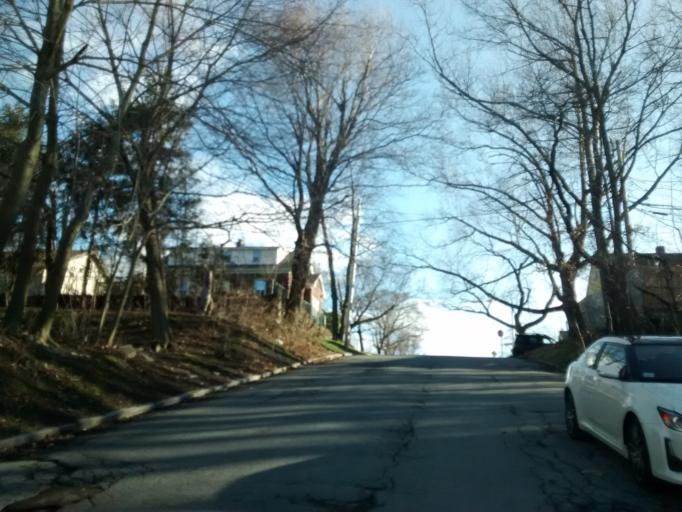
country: US
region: Massachusetts
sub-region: Worcester County
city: Worcester
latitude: 42.2926
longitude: -71.8096
